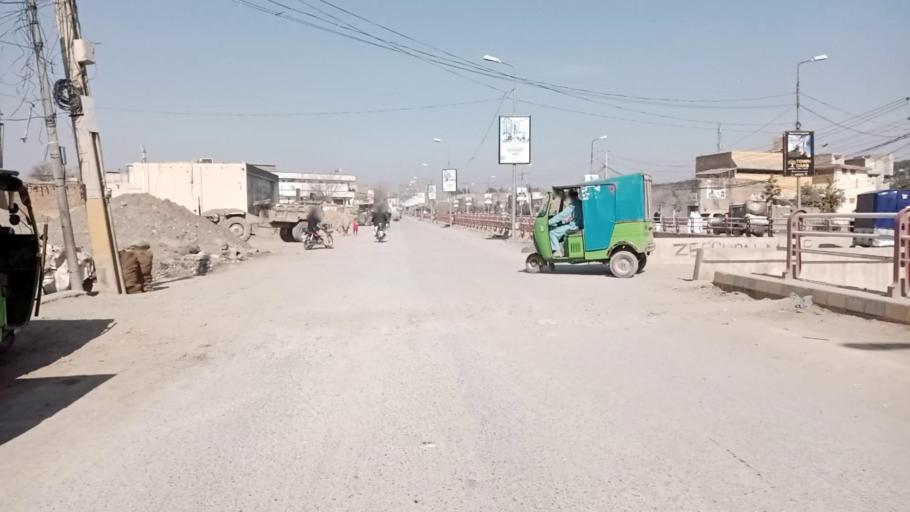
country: PK
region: Khyber Pakhtunkhwa
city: Peshawar
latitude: 33.9851
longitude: 71.4985
